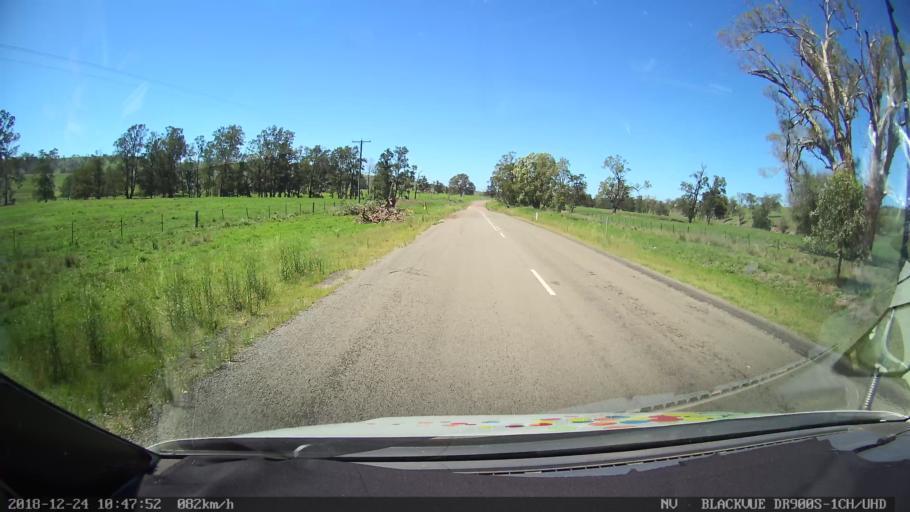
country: AU
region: New South Wales
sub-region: Upper Hunter Shire
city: Merriwa
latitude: -31.9295
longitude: 150.4298
